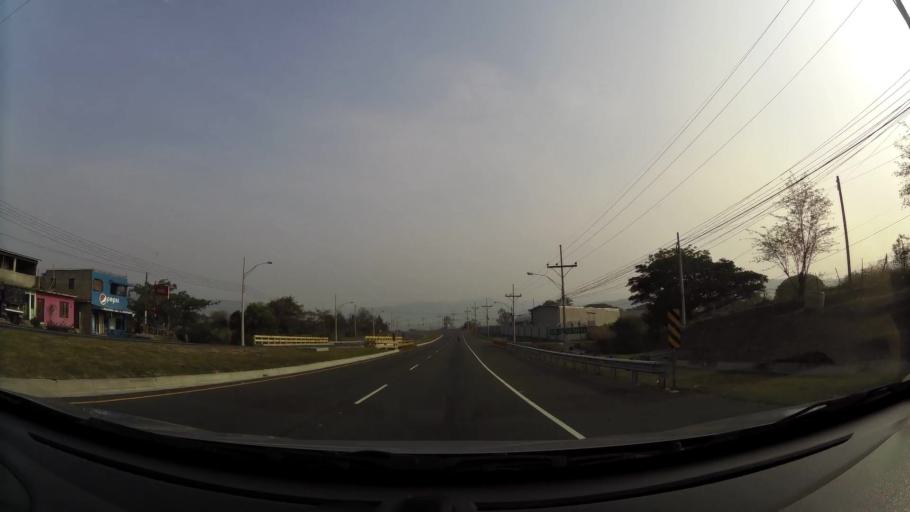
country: HN
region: Francisco Morazan
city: Tamara
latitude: 14.2111
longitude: -87.3527
